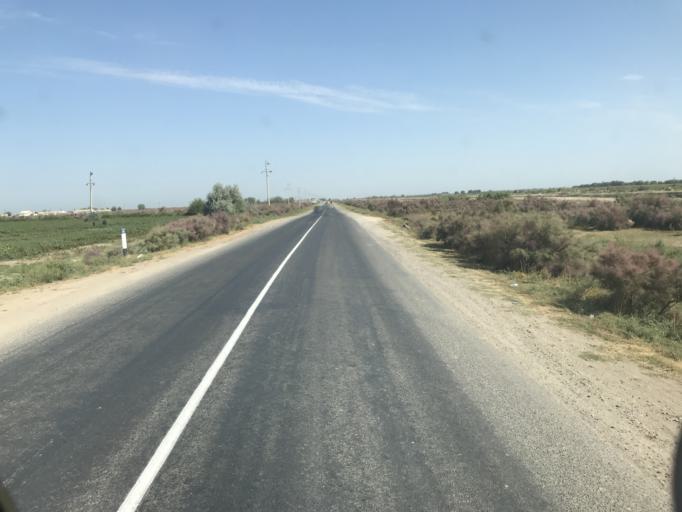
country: KZ
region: Ongtustik Qazaqstan
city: Myrzakent
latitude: 40.6805
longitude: 68.5321
